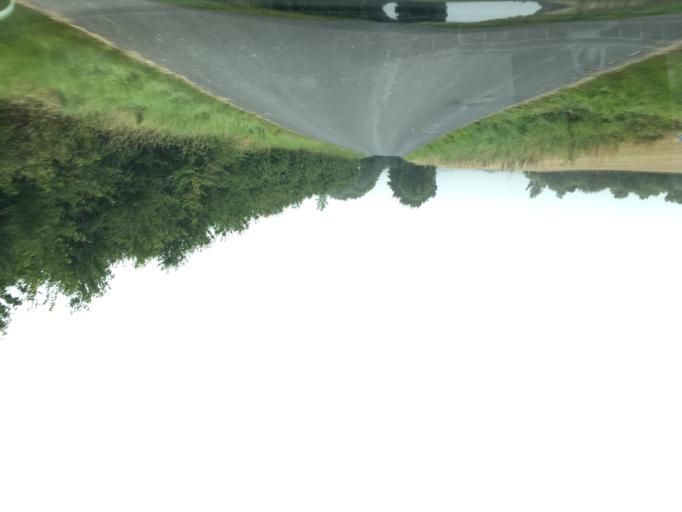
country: DK
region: South Denmark
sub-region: Kolding Kommune
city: Kolding
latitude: 55.5628
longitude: 9.4412
